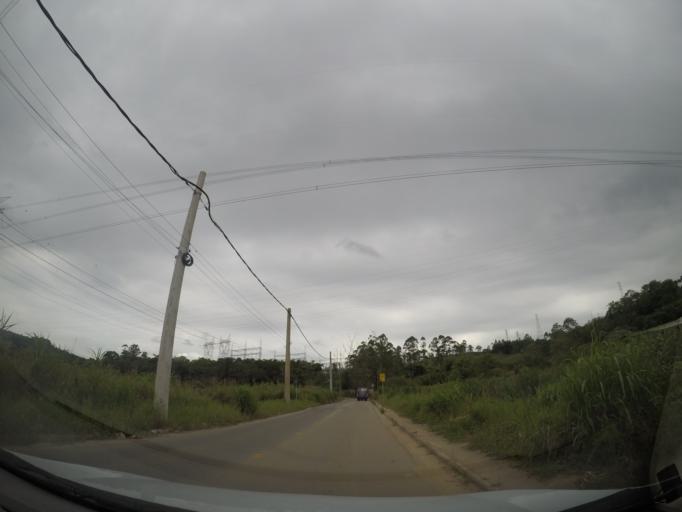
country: BR
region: Sao Paulo
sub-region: Aruja
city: Aruja
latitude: -23.3706
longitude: -46.4012
